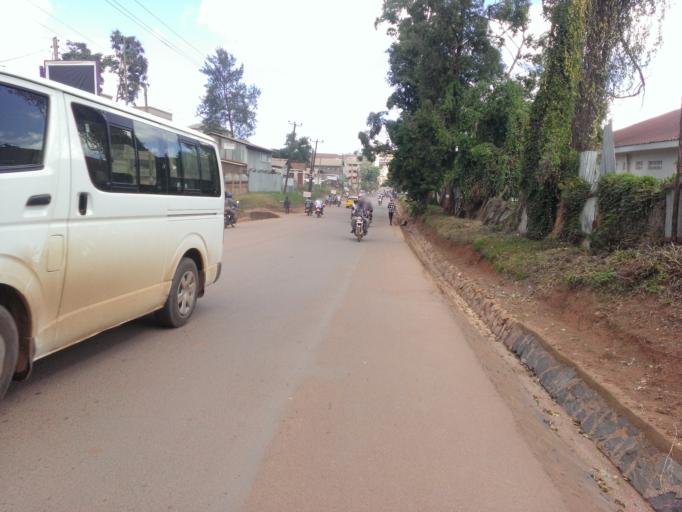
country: UG
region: Central Region
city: Kampala Central Division
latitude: 0.3250
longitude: 32.5698
